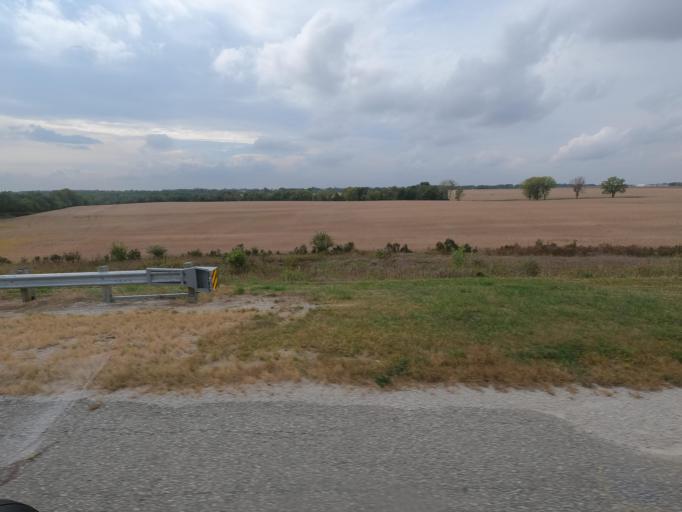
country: US
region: Iowa
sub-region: Wapello County
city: Ottumwa
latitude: 41.0766
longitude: -92.3940
